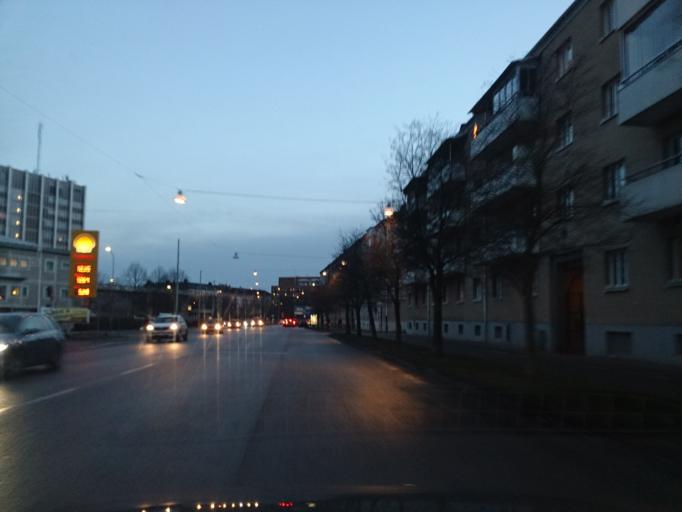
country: SE
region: OEstergoetland
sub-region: Norrkopings Kommun
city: Norrkoping
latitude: 58.5963
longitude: 16.1725
